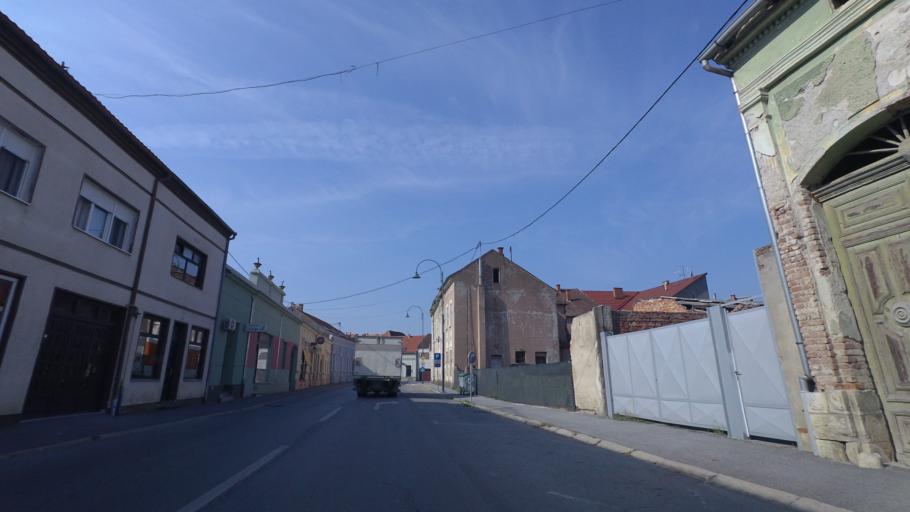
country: HR
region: Pozesko-Slavonska
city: Pakrac
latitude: 45.4385
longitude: 17.1937
